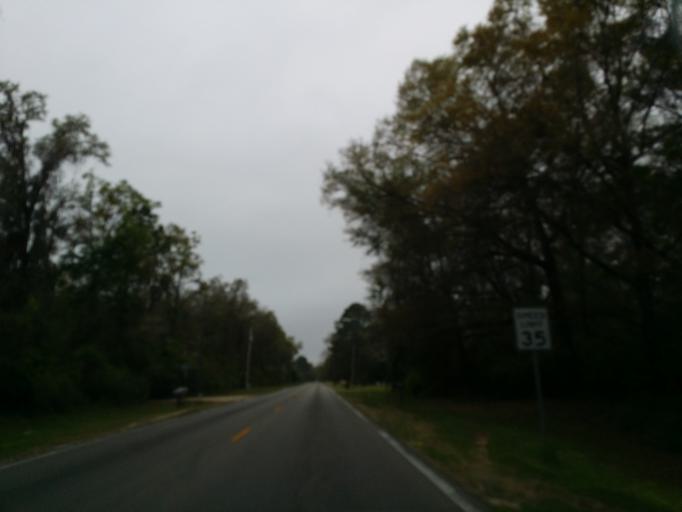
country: US
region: Florida
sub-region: Leon County
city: Woodville
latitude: 30.3214
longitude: -84.2573
